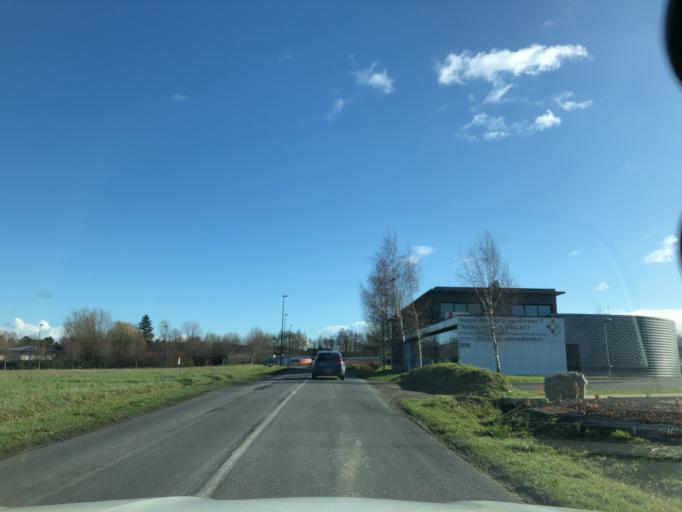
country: FR
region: Lower Normandy
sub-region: Departement du Calvados
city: Epron
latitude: 49.2193
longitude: -0.3558
